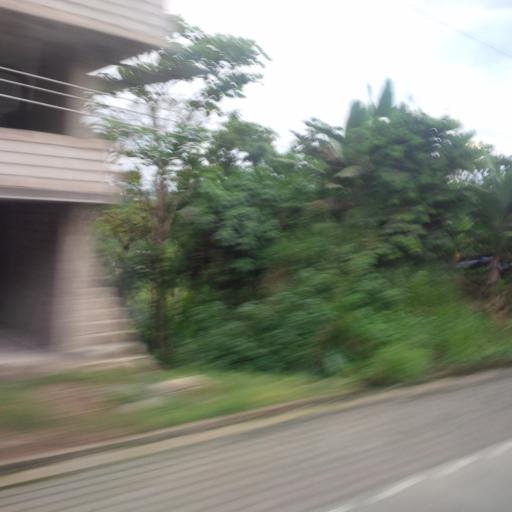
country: EC
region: Chimborazo
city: Alausi
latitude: -2.2007
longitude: -79.1222
